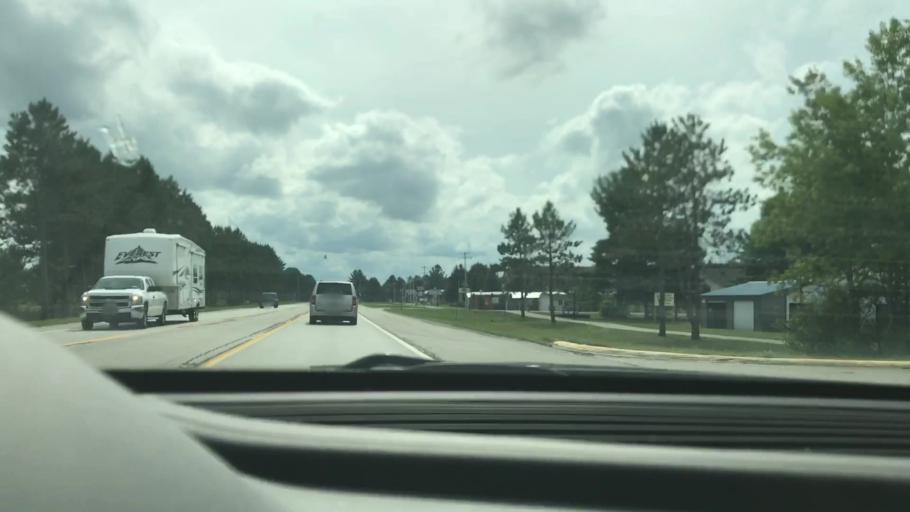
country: US
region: Michigan
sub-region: Kalkaska County
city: Kalkaska
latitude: 44.7243
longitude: -85.1838
